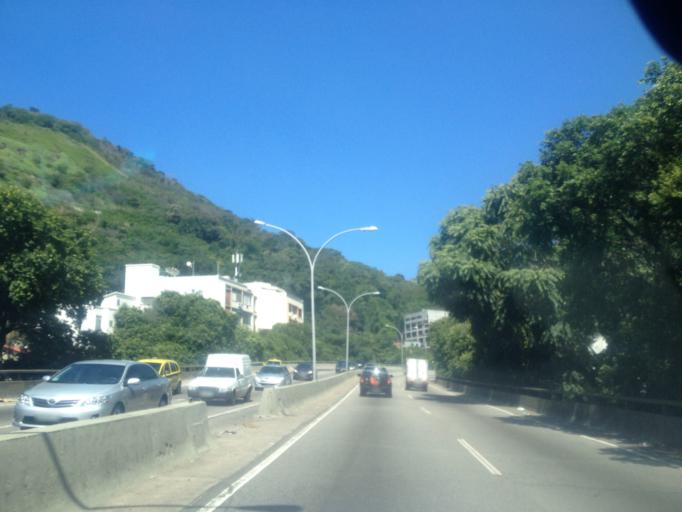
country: BR
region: Rio de Janeiro
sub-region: Rio De Janeiro
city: Rio de Janeiro
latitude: -22.9298
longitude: -43.2091
